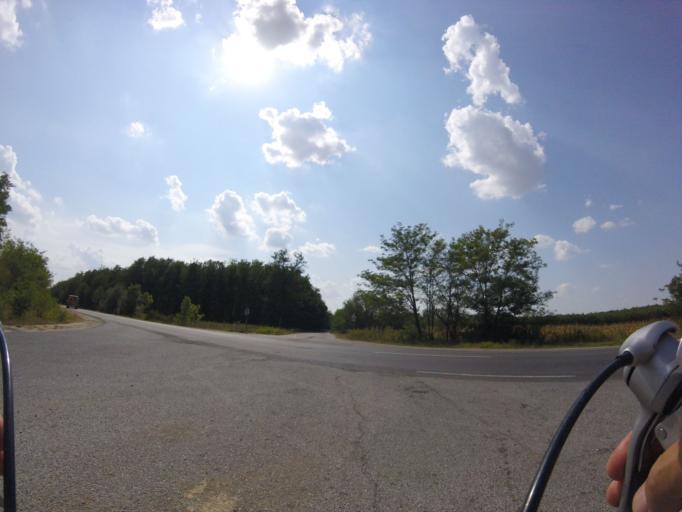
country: HU
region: Szabolcs-Szatmar-Bereg
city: Nyirtass
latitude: 48.1053
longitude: 21.9882
